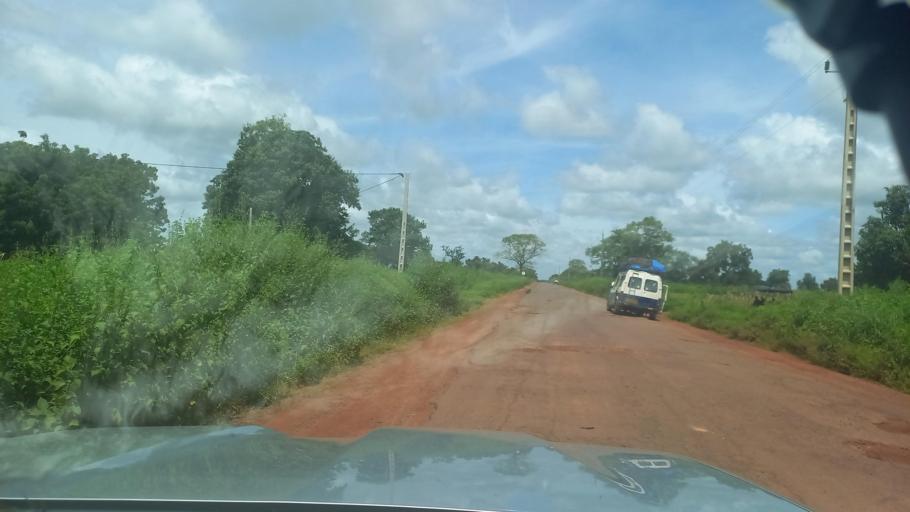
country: GM
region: Lower River
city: Kaiaf
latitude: 13.2227
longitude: -15.5404
